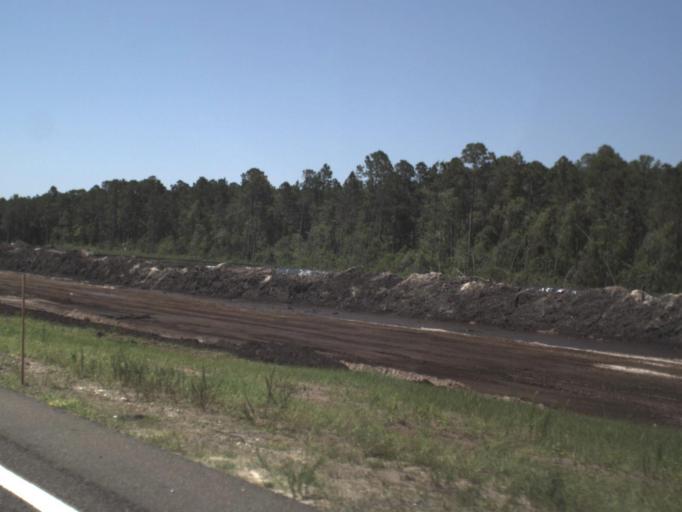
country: US
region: Florida
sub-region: Duval County
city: Baldwin
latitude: 30.2583
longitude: -81.8585
